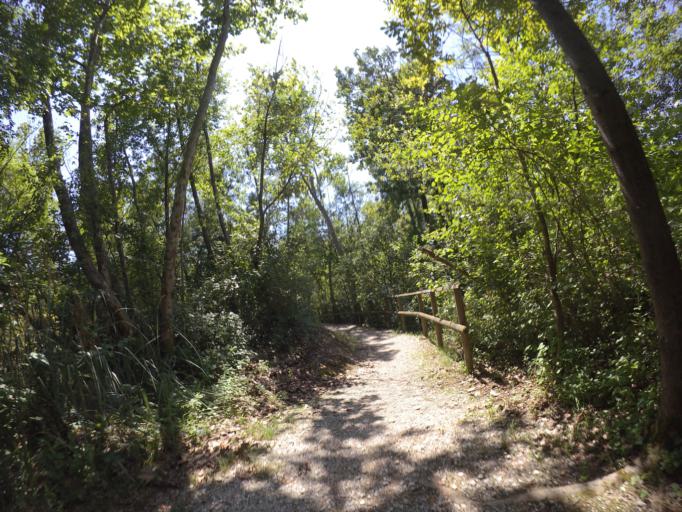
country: IT
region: Friuli Venezia Giulia
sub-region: Provincia di Udine
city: Bertiolo
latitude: 45.9182
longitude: 13.0755
